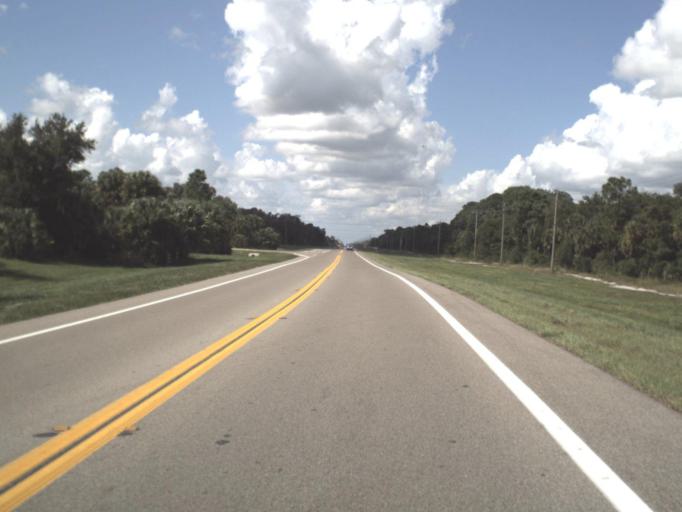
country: US
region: Florida
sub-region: Lee County
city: Lehigh Acres
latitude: 26.5531
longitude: -81.6477
